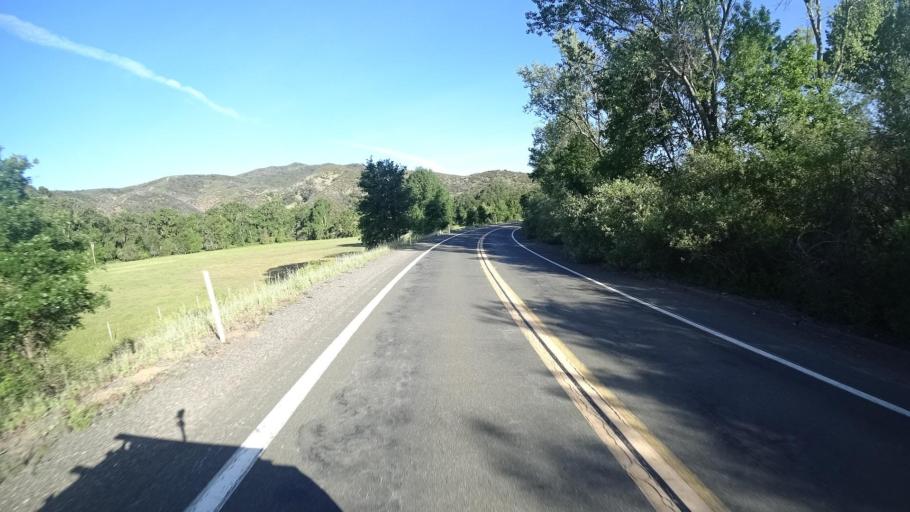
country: US
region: California
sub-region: Lake County
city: North Lakeport
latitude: 39.1065
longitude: -122.9738
